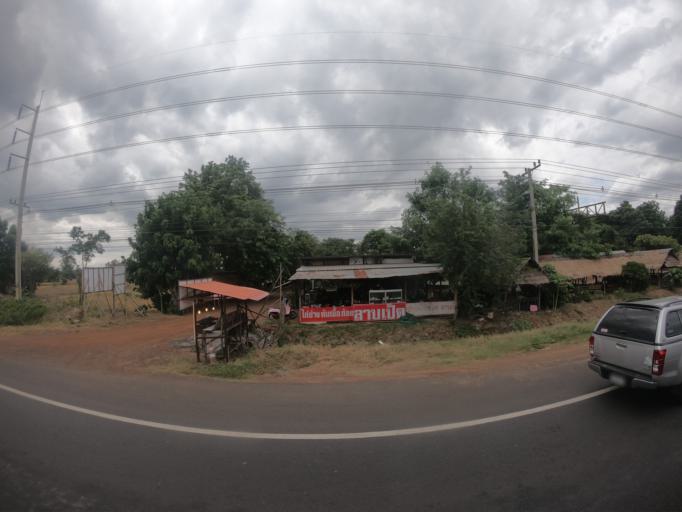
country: TH
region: Buriram
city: Nong Ki
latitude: 14.6998
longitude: 102.4919
